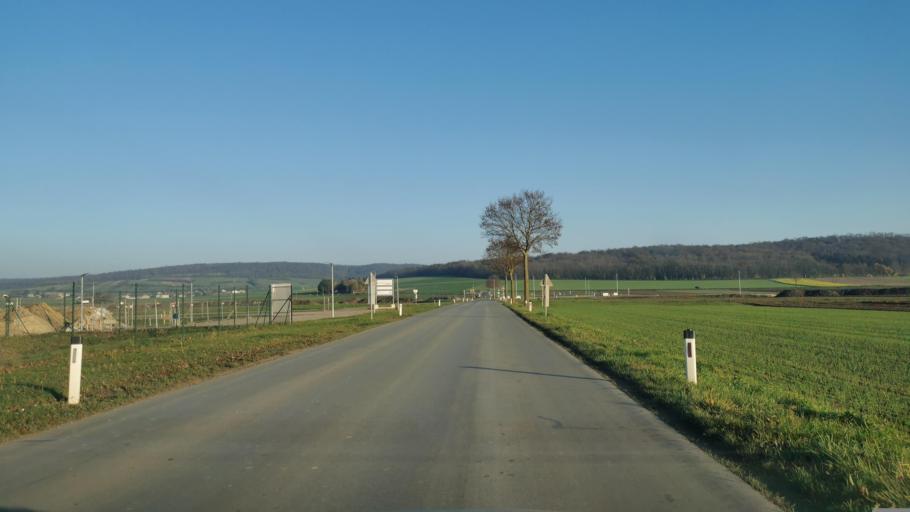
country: AT
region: Lower Austria
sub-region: Politischer Bezirk Korneuburg
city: Harmannsdorf
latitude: 48.3904
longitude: 16.3831
